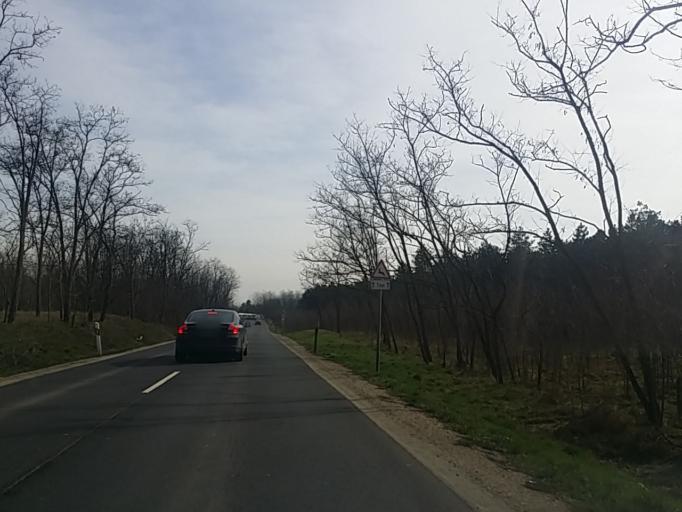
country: HU
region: Pest
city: Fot
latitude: 47.6357
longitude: 19.2157
